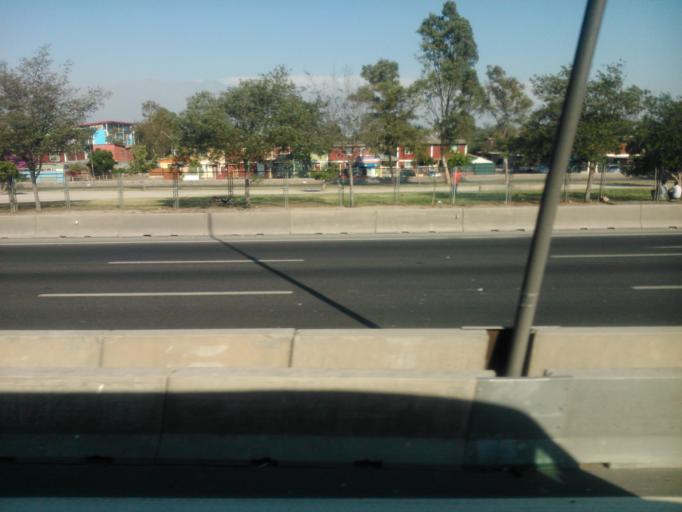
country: CL
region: Santiago Metropolitan
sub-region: Provincia de Santiago
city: Santiago
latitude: -33.4907
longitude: -70.6900
